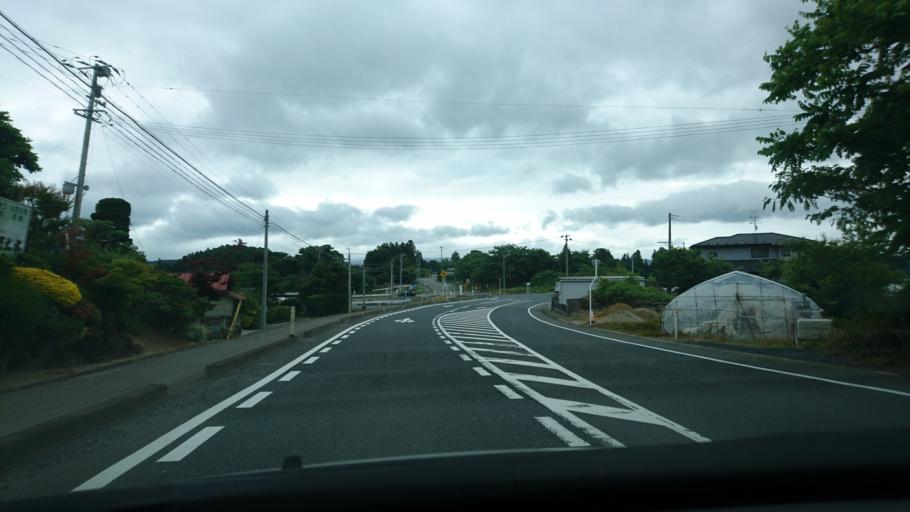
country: JP
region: Iwate
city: Ichinoseki
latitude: 38.7476
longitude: 141.2552
